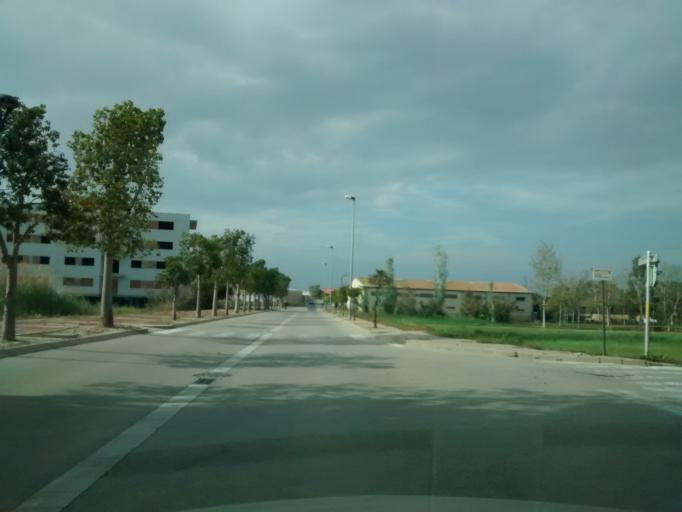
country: ES
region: Catalonia
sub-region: Provincia de Tarragona
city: Deltebre
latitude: 40.7222
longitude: 0.7210
